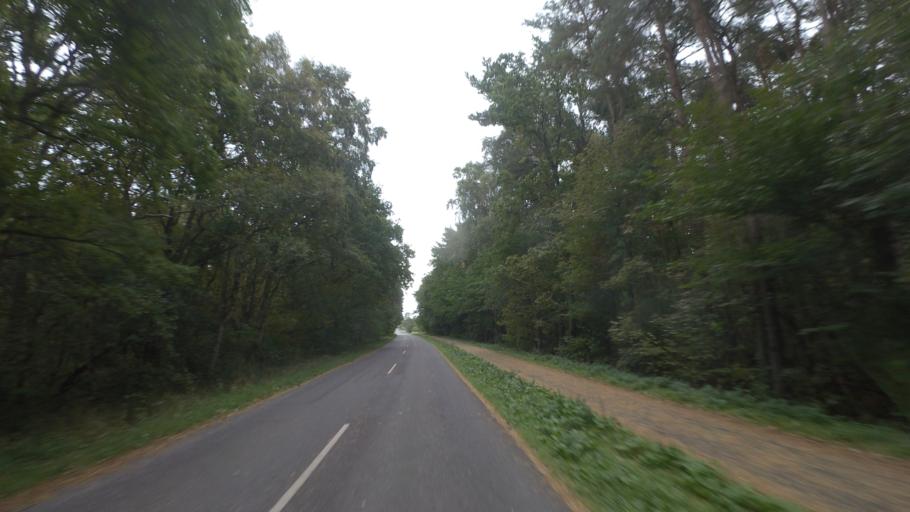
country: DK
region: Capital Region
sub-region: Bornholm Kommune
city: Nexo
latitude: 55.0030
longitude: 15.0431
